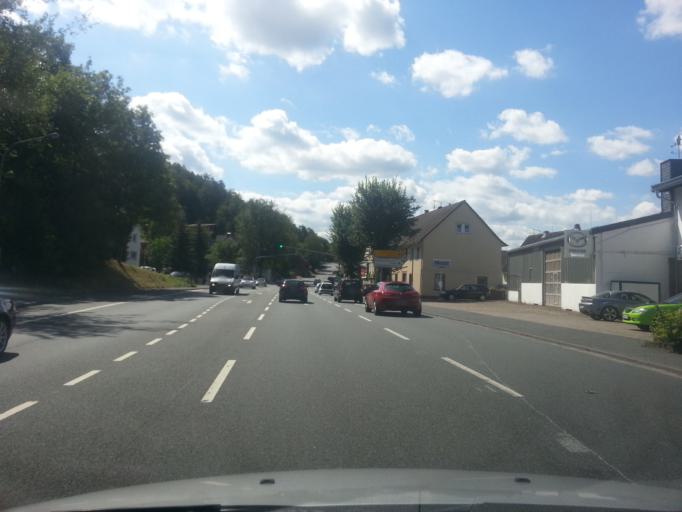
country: DE
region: Hesse
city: Hochst im Odenwald
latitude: 49.7725
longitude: 8.9916
